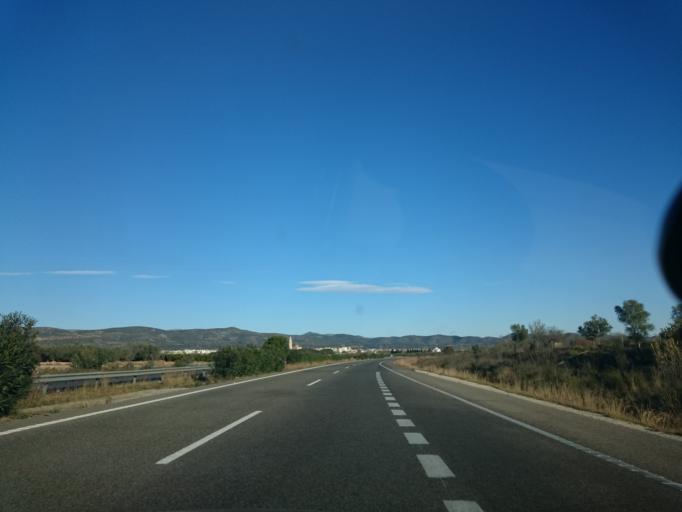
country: ES
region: Valencia
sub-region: Provincia de Castello
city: Alcala de Xivert
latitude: 40.2867
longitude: 0.2284
